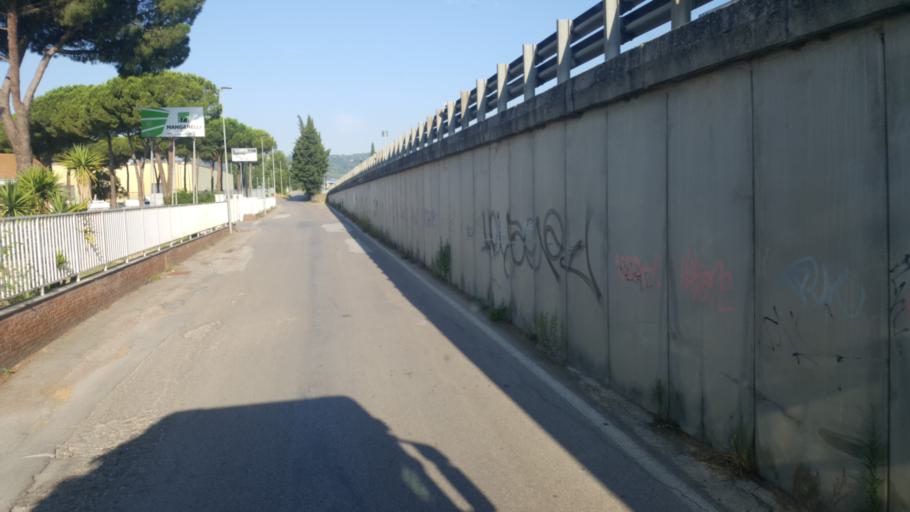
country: IT
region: Umbria
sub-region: Provincia di Perugia
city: Via Lippia
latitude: 43.0857
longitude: 12.4403
